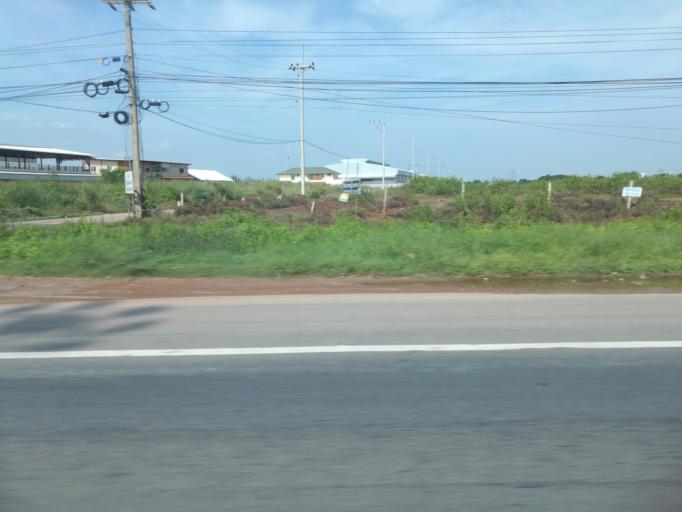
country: TH
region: Samut Songkhram
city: Samut Songkhram
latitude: 13.4434
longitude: 100.0696
